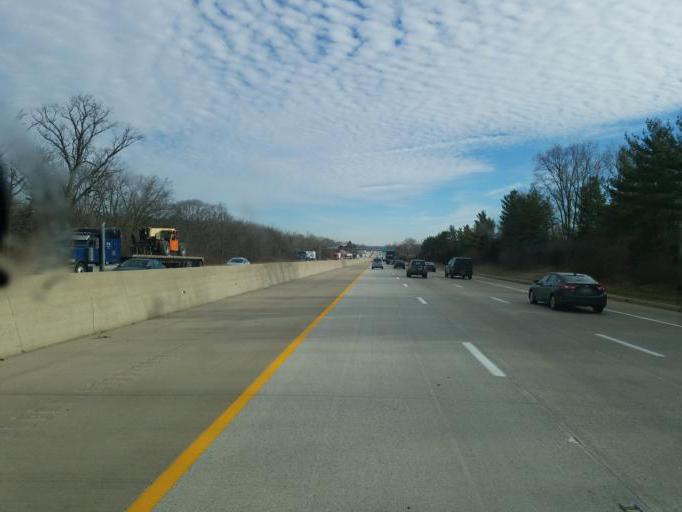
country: US
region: Ohio
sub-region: Montgomery County
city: Huber Heights
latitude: 39.8670
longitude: -84.0892
